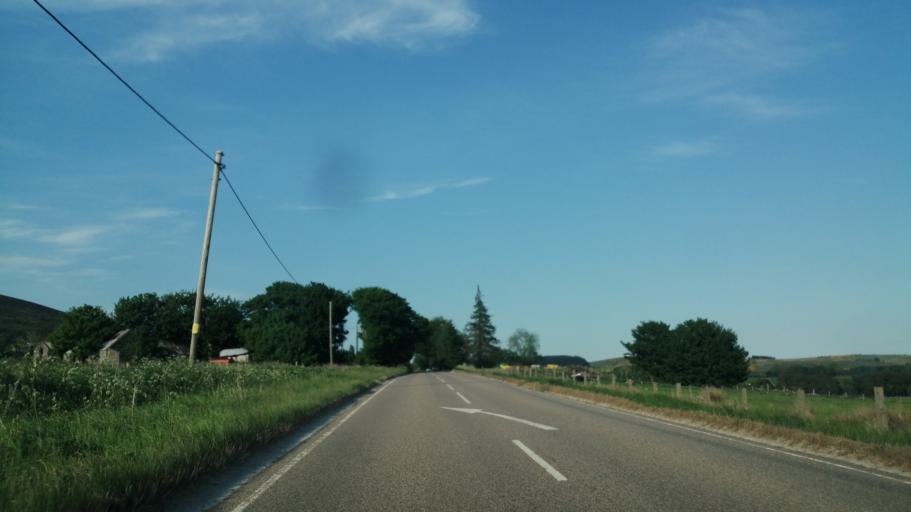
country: GB
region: Scotland
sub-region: Aberdeenshire
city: Huntly
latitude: 57.5667
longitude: -2.7877
